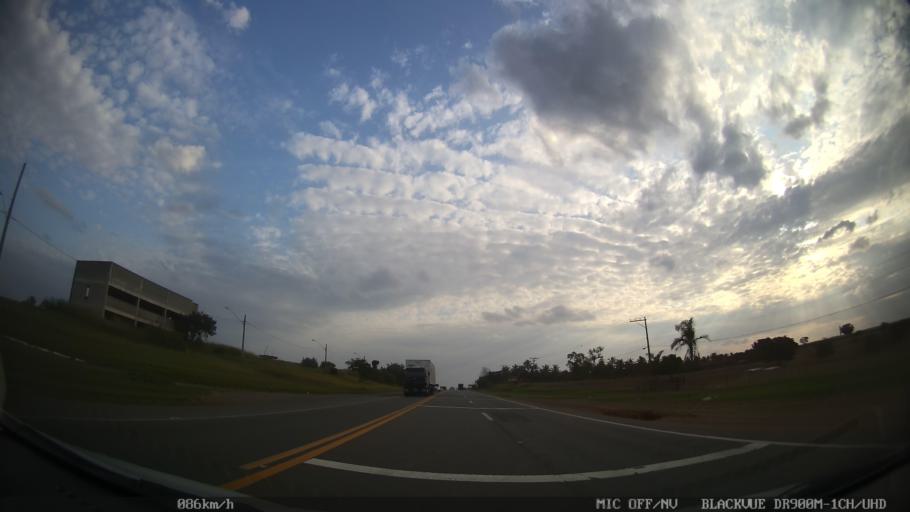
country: BR
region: Sao Paulo
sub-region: Americana
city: Americana
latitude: -22.6356
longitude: -47.3151
